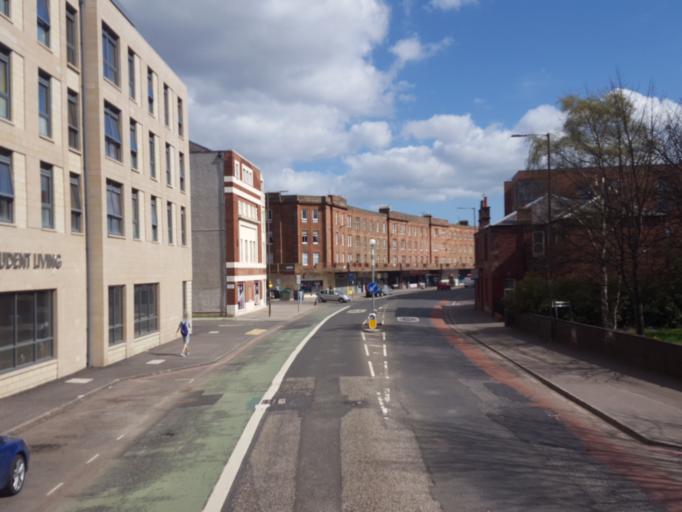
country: GB
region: Scotland
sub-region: Edinburgh
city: Colinton
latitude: 55.9357
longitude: -3.2421
